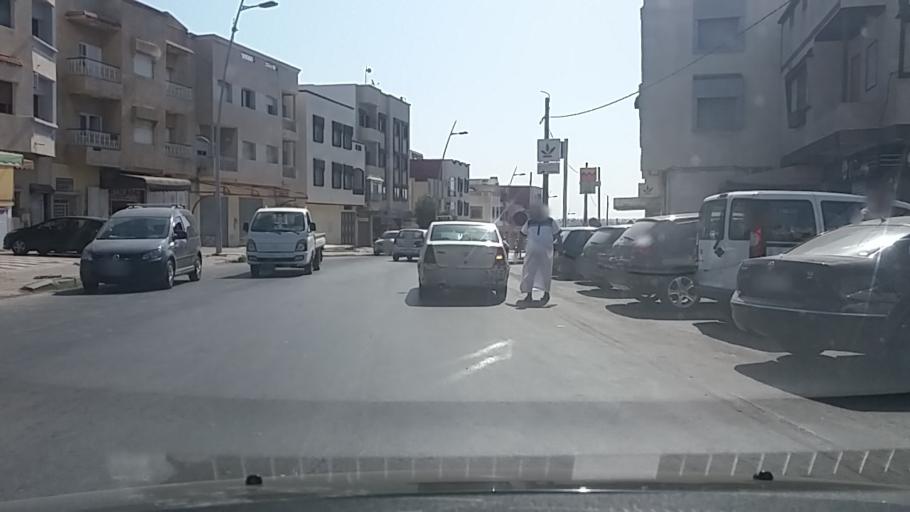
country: MA
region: Gharb-Chrarda-Beni Hssen
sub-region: Kenitra Province
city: Kenitra
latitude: 34.2660
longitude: -6.6156
